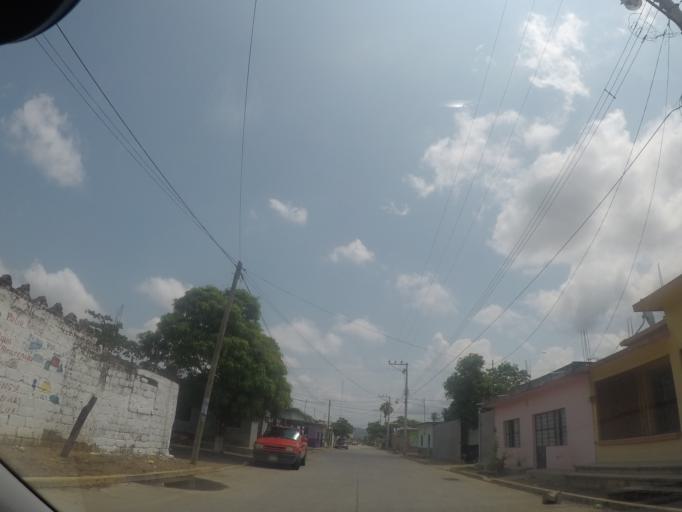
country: MX
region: Oaxaca
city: El Espinal
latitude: 16.5507
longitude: -94.9472
